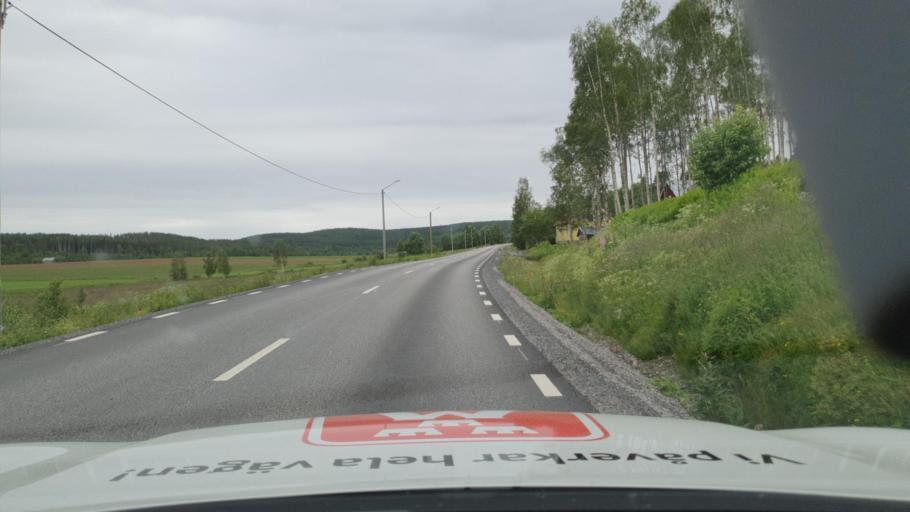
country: SE
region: Vaesterbotten
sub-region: Vannas Kommun
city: Vaennaes
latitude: 63.7431
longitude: 19.6501
